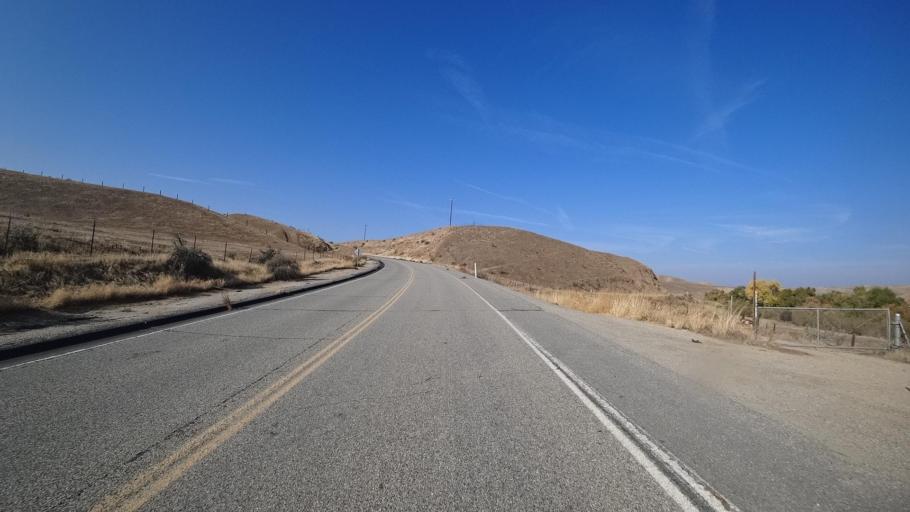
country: US
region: California
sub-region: Kern County
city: Oildale
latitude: 35.5276
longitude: -118.9726
